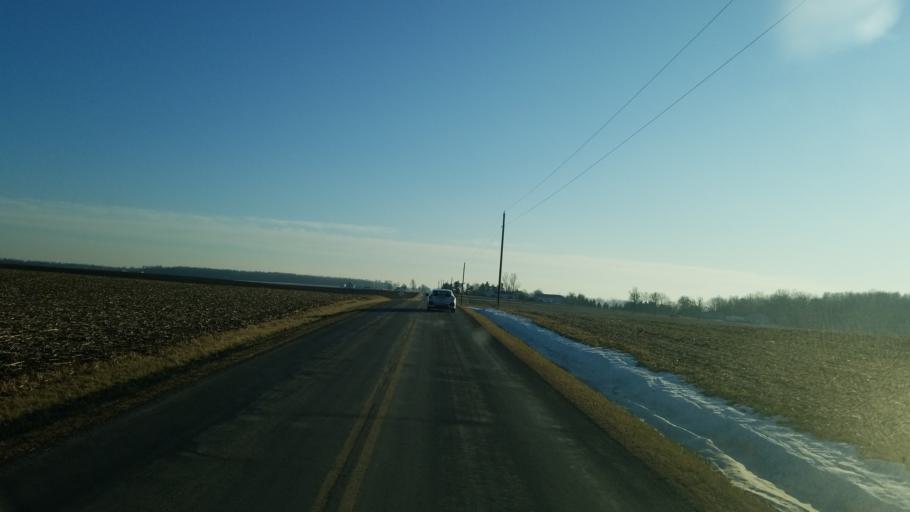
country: US
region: Ohio
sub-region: Crawford County
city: Bucyrus
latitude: 40.8986
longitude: -82.9018
